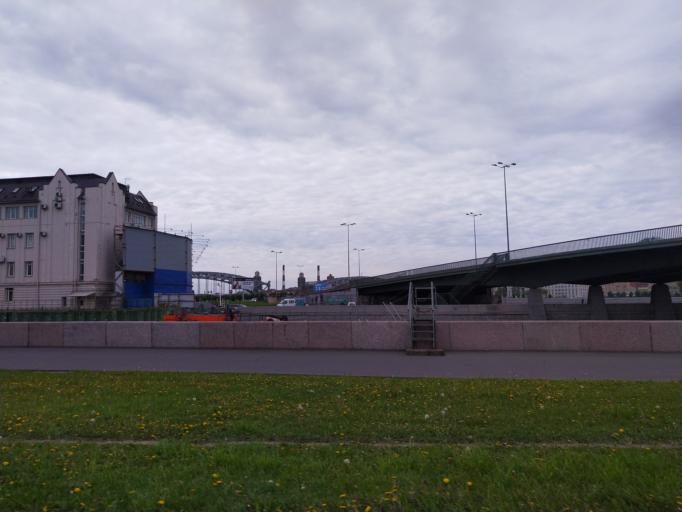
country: RU
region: Leningrad
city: Finlyandskiy
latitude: 59.9465
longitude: 30.4073
